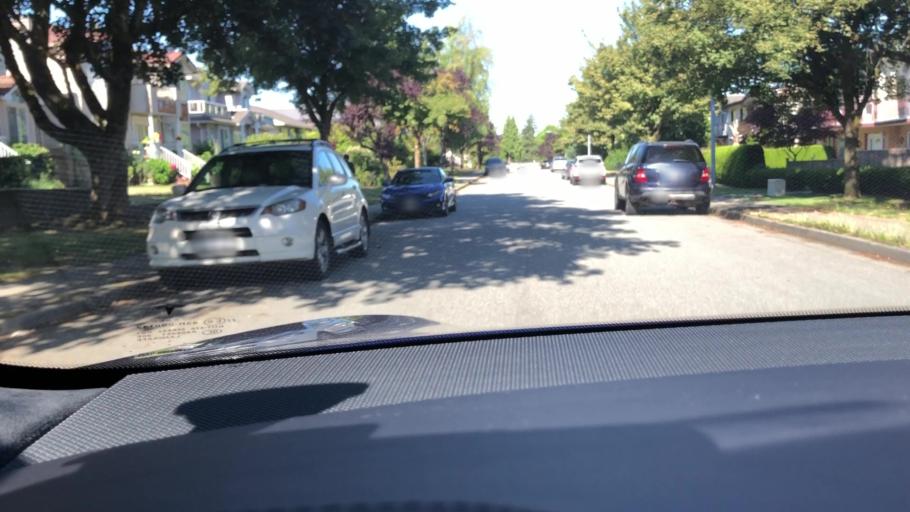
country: CA
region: British Columbia
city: Burnaby
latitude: 49.2211
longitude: -122.9678
